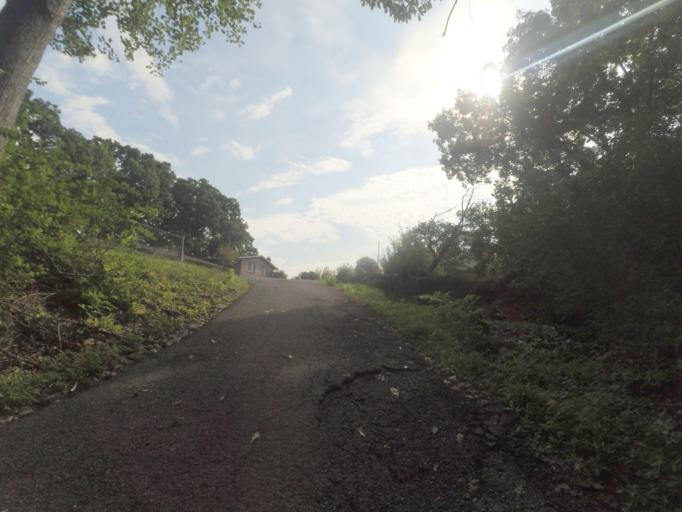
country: US
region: West Virginia
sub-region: Cabell County
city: Huntington
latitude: 38.4000
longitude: -82.4219
